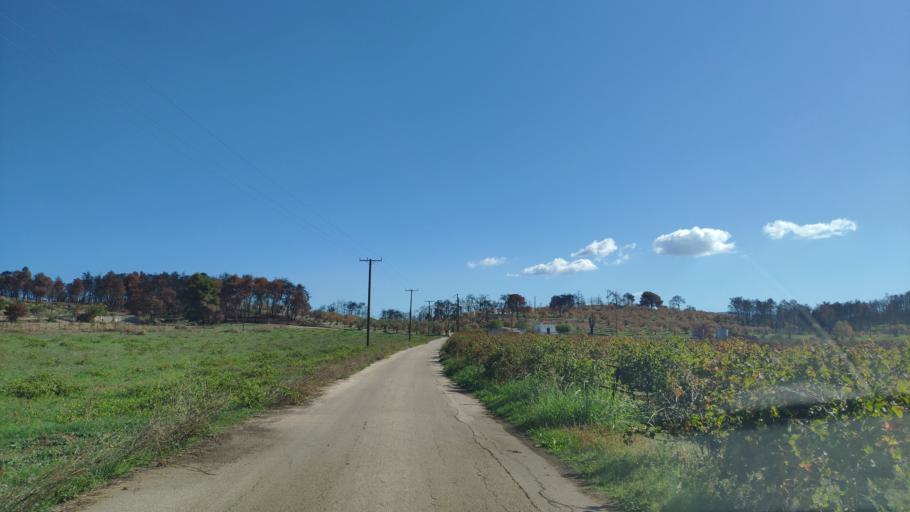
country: GR
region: Peloponnese
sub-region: Nomos Korinthias
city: Athikia
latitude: 37.8449
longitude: 22.9480
